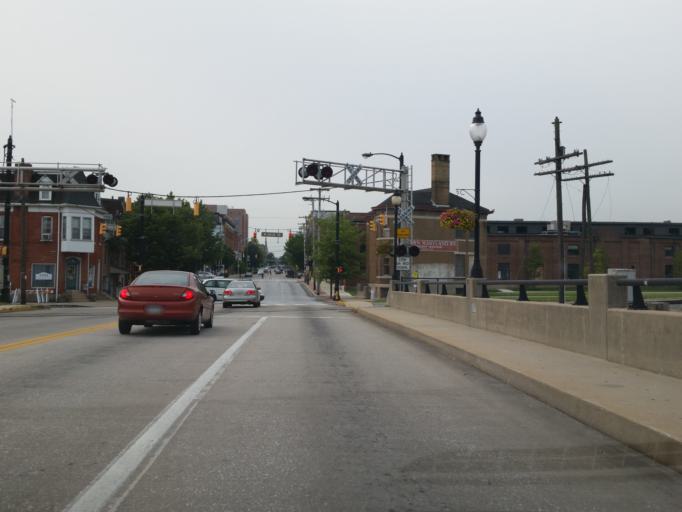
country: US
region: Pennsylvania
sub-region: York County
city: York
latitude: 39.9679
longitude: -76.7306
